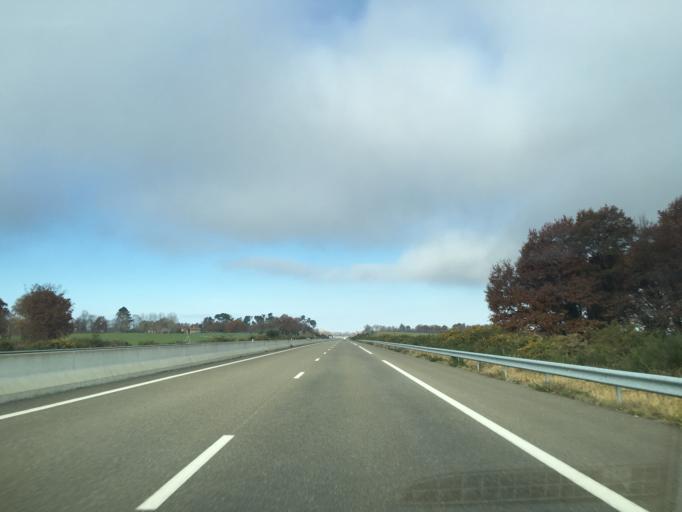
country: FR
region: Aquitaine
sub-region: Departement des Landes
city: Villeneuve-de-Marsan
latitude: 43.8373
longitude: -0.3264
